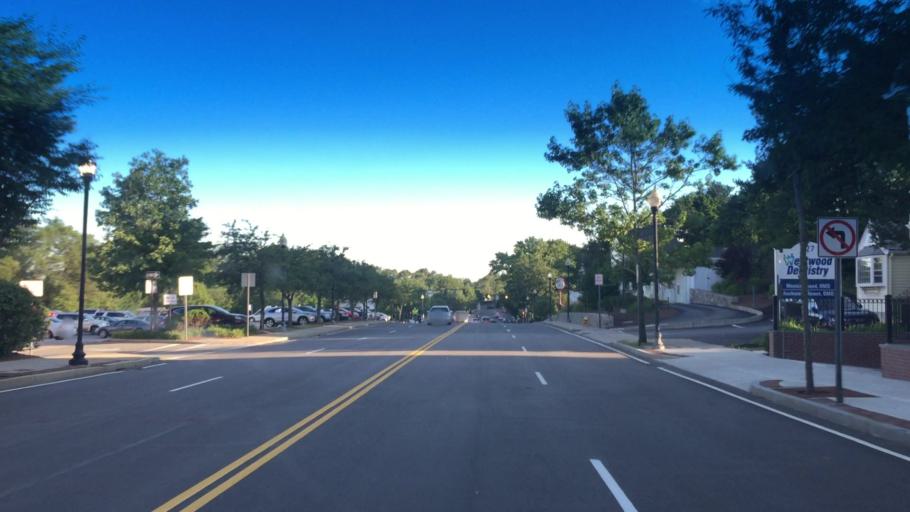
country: US
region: Massachusetts
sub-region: Norfolk County
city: Norwood
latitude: 42.2181
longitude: -71.1884
